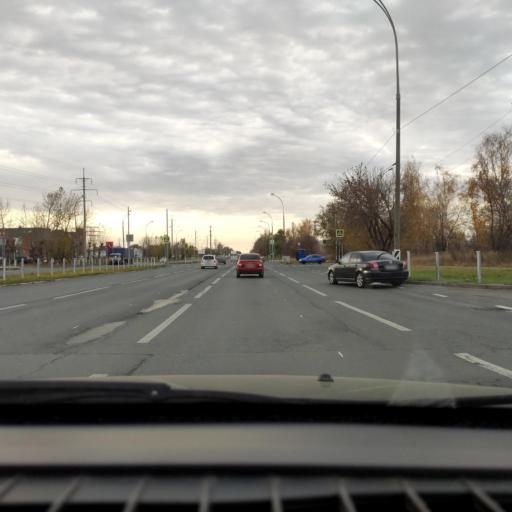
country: RU
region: Samara
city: Tol'yatti
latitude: 53.5518
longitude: 49.2869
